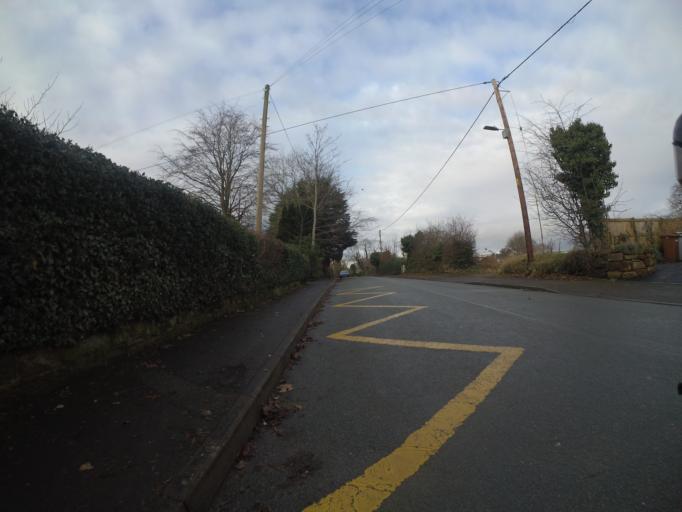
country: GB
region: England
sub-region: Cheshire West and Chester
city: Tiverton
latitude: 53.1174
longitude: -2.6555
